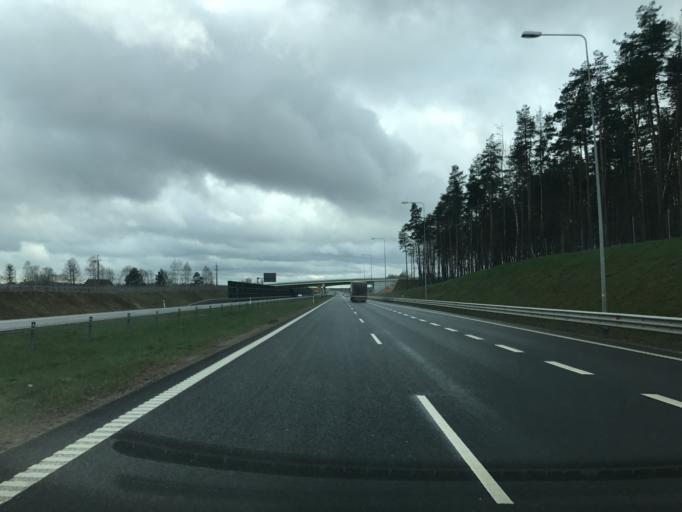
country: PL
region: Warmian-Masurian Voivodeship
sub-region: Powiat olsztynski
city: Olsztynek
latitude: 53.6033
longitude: 20.2998
